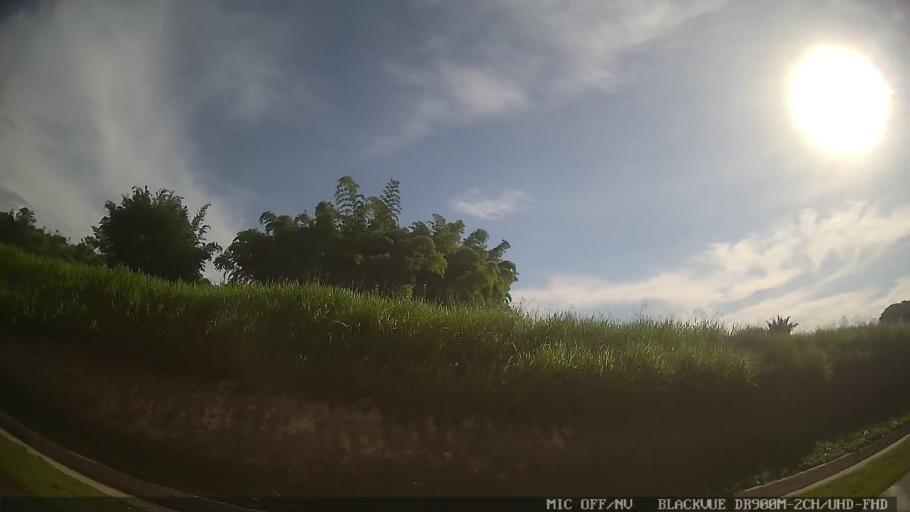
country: BR
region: Sao Paulo
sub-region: Tiete
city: Tiete
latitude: -23.1201
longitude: -47.7015
